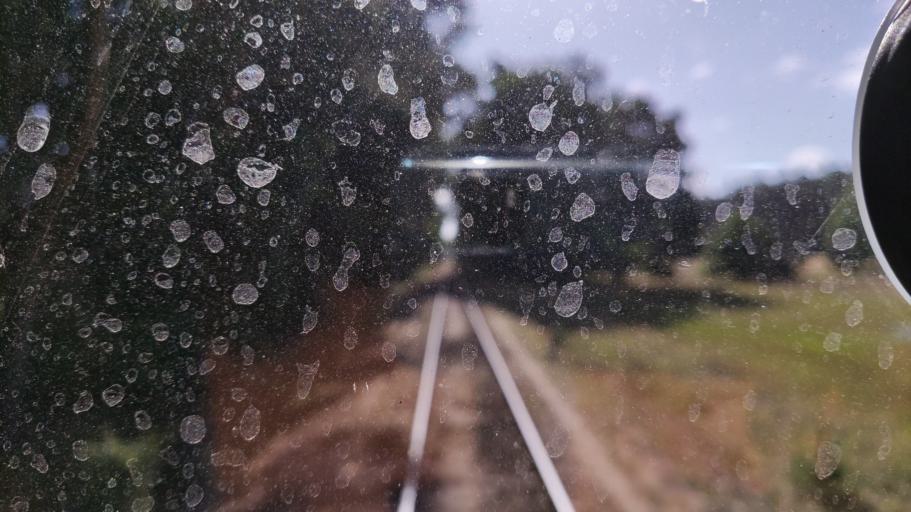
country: DE
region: Lower Saxony
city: Neetze
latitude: 53.2783
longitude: 10.5979
